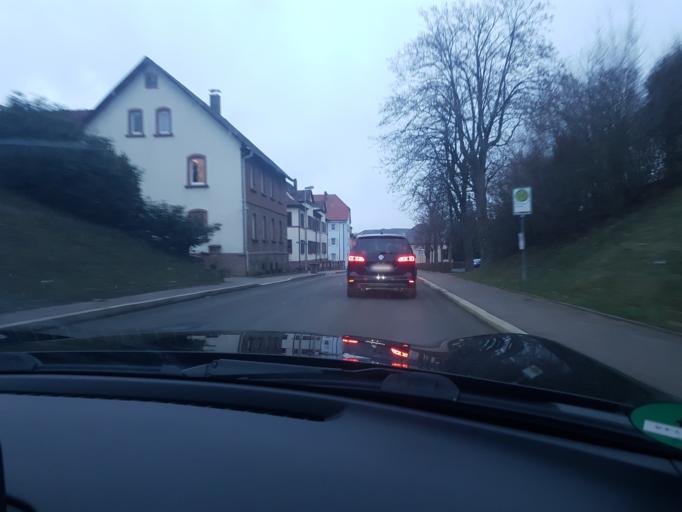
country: DE
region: Baden-Wuerttemberg
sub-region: Karlsruhe Region
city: Buchen
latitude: 49.5189
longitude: 9.3229
